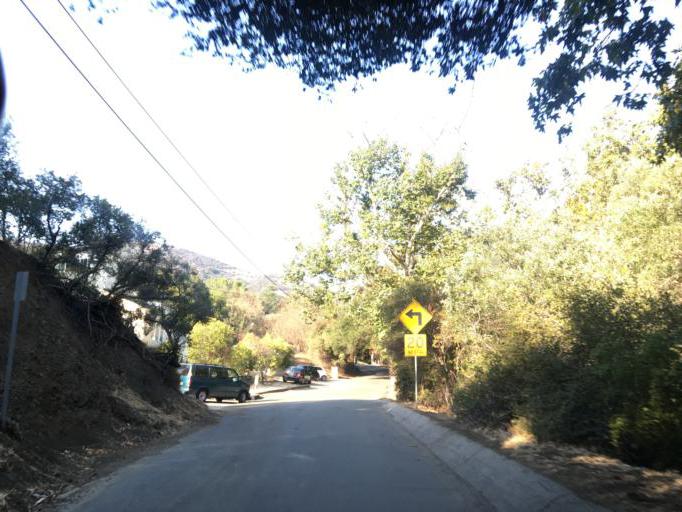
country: US
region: California
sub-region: Los Angeles County
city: Malibu Beach
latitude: 34.0820
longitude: -118.6873
